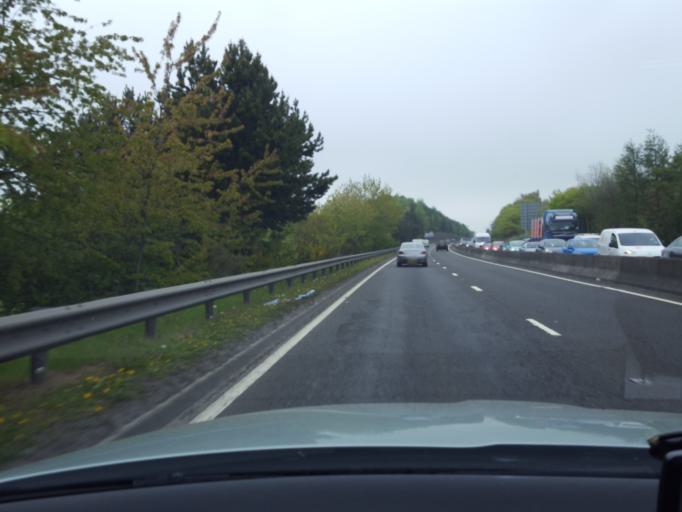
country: GB
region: Scotland
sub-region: Dundee City
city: Dundee
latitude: 56.4973
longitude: -2.9502
